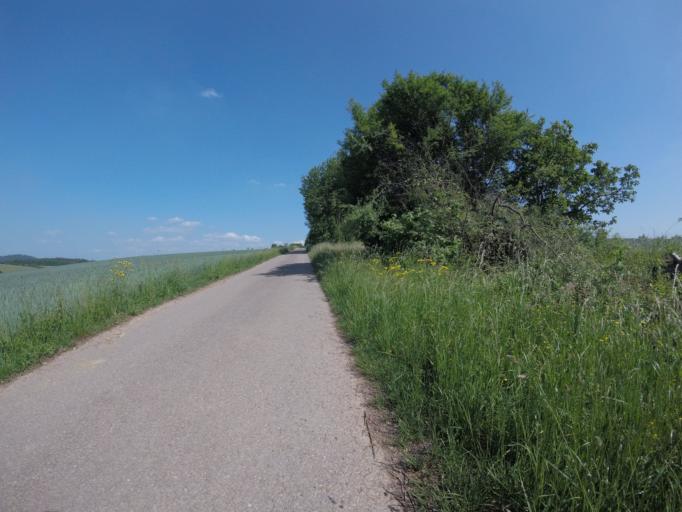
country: DE
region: Baden-Wuerttemberg
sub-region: Regierungsbezirk Stuttgart
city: Steinheim am der Murr
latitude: 48.9726
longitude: 9.2984
